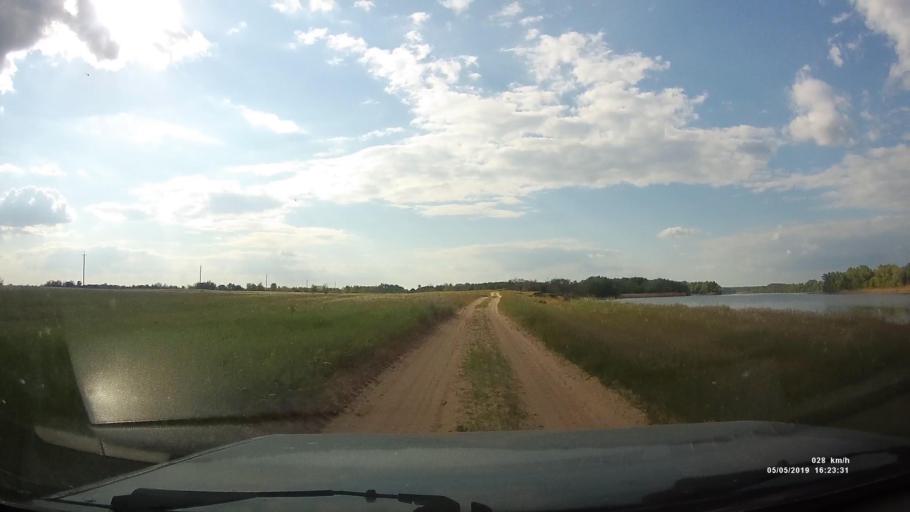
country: RU
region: Rostov
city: Konstantinovsk
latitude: 47.7569
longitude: 41.0300
